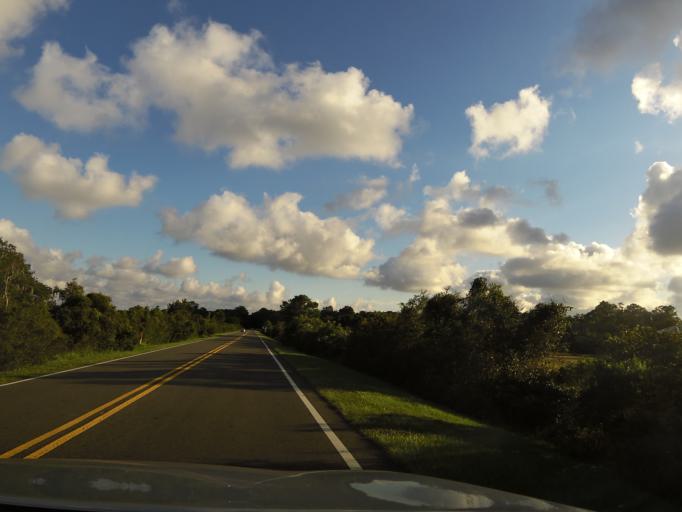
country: US
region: Georgia
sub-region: Glynn County
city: Saint Simon Mills
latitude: 31.1848
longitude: -81.3989
